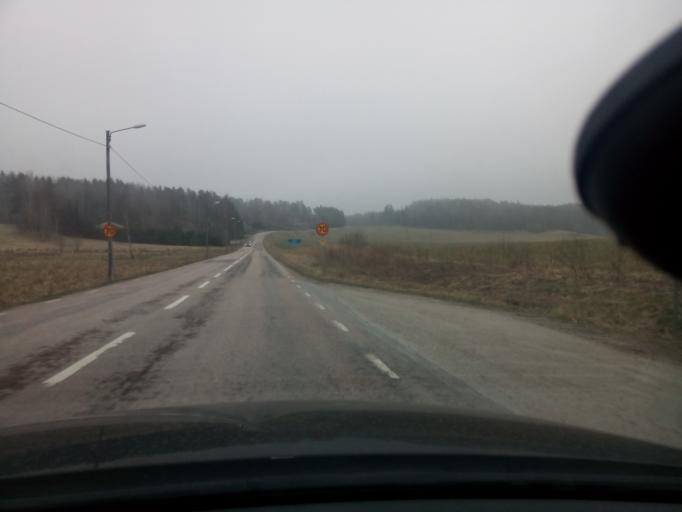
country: SE
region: Soedermanland
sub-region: Nykopings Kommun
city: Nykoping
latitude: 58.9258
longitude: 17.0999
